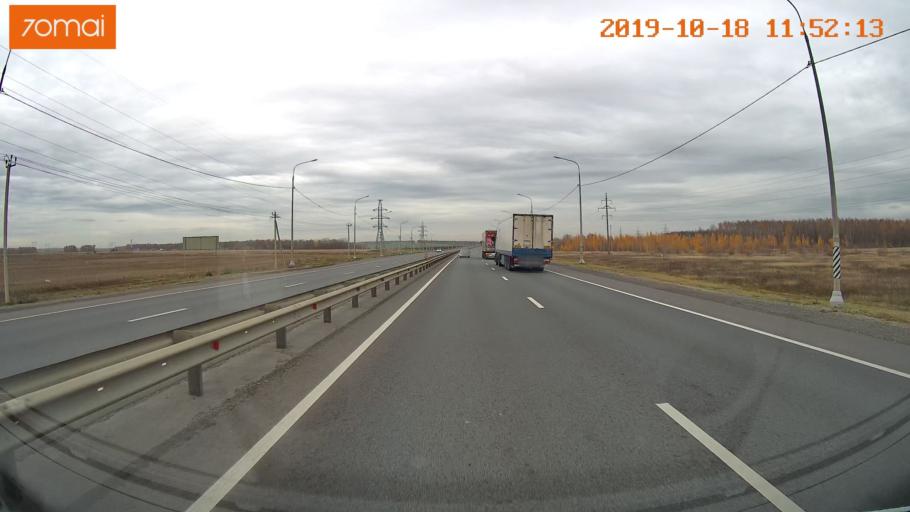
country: RU
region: Rjazan
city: Mikhaylov
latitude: 54.2500
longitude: 39.0433
